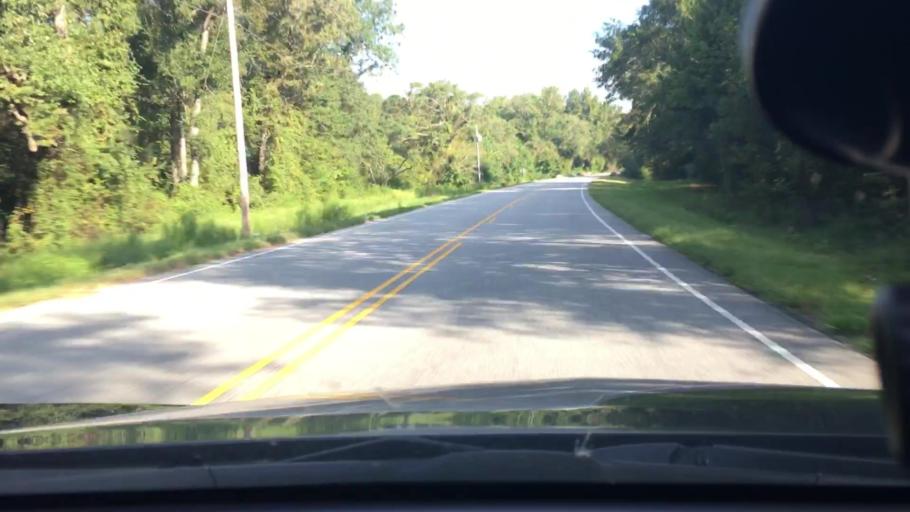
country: US
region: North Carolina
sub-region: Edgecombe County
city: Pinetops
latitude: 35.7206
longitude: -77.5293
